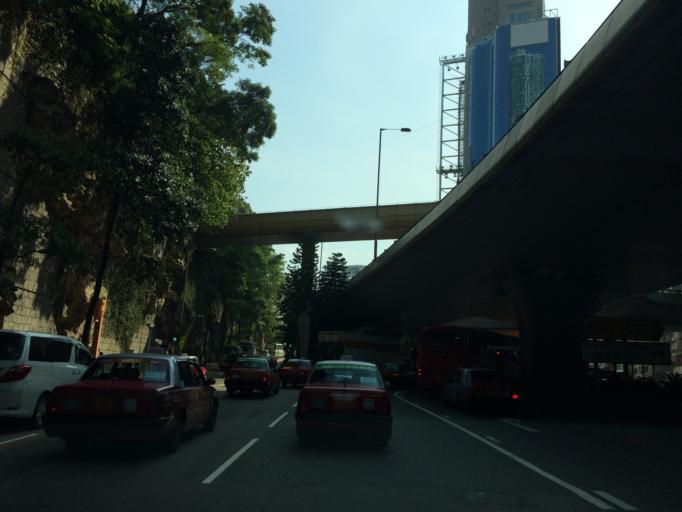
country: HK
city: Hong Kong
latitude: 22.3005
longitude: 114.1683
